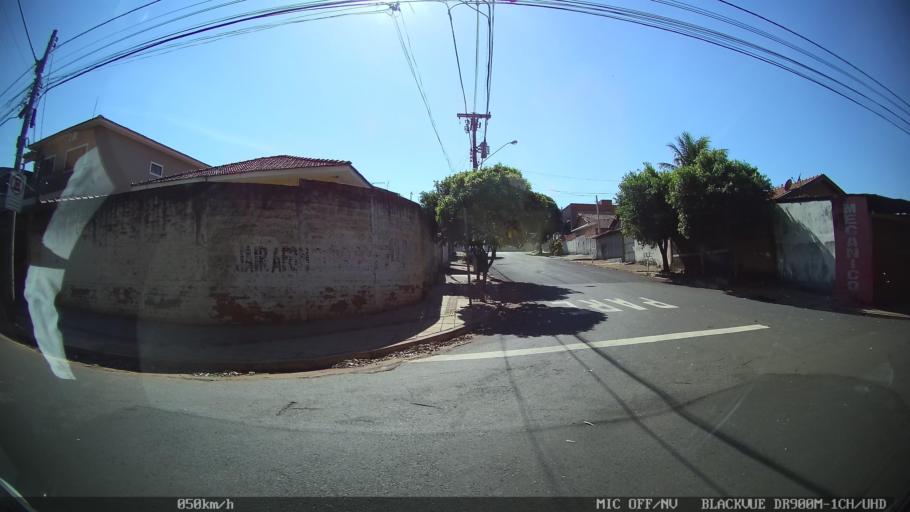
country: BR
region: Sao Paulo
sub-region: Sao Jose Do Rio Preto
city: Sao Jose do Rio Preto
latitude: -20.7773
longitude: -49.3907
